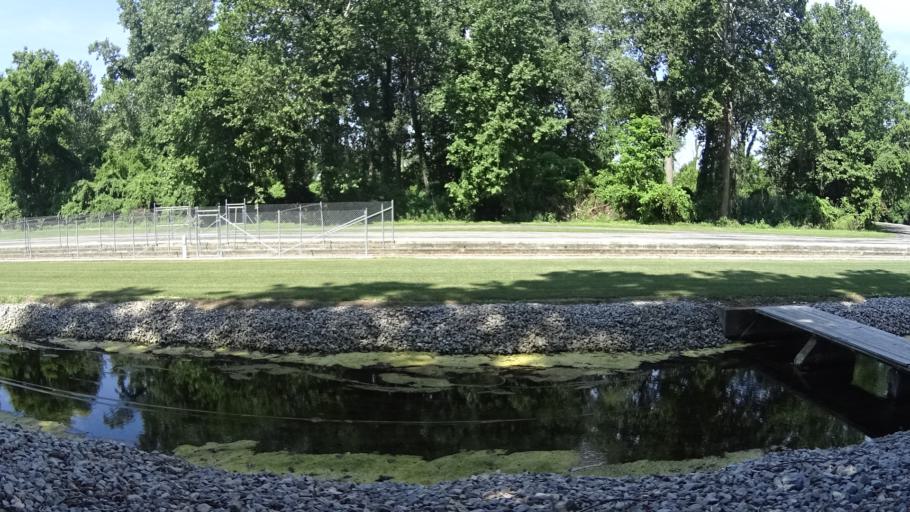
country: US
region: Ohio
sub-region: Erie County
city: Sandusky
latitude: 41.4171
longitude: -82.8067
